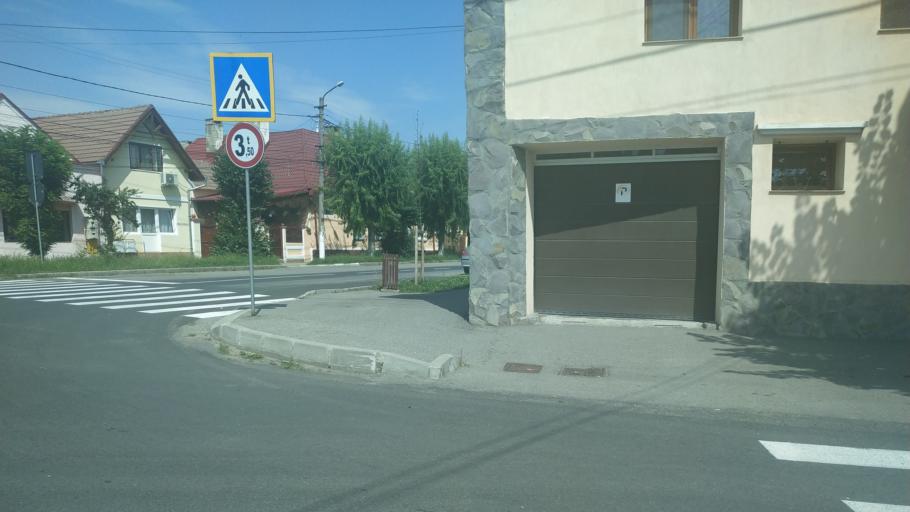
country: RO
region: Brasov
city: Fogarasch
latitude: 45.8418
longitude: 24.9655
